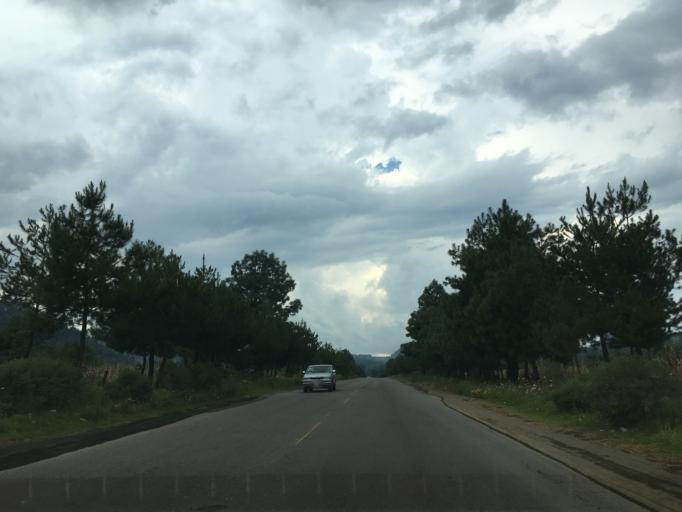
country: MX
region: Michoacan
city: Angahuan
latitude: 19.5370
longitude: -102.1973
